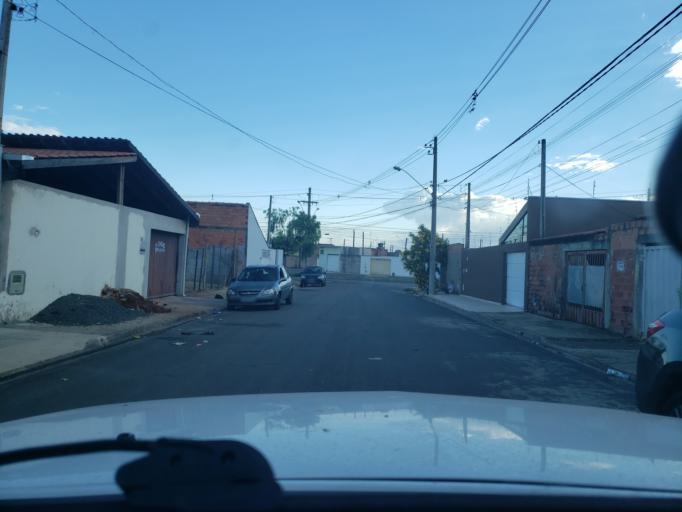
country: BR
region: Sao Paulo
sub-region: Moji-Guacu
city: Mogi-Gaucu
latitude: -22.3297
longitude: -46.9252
